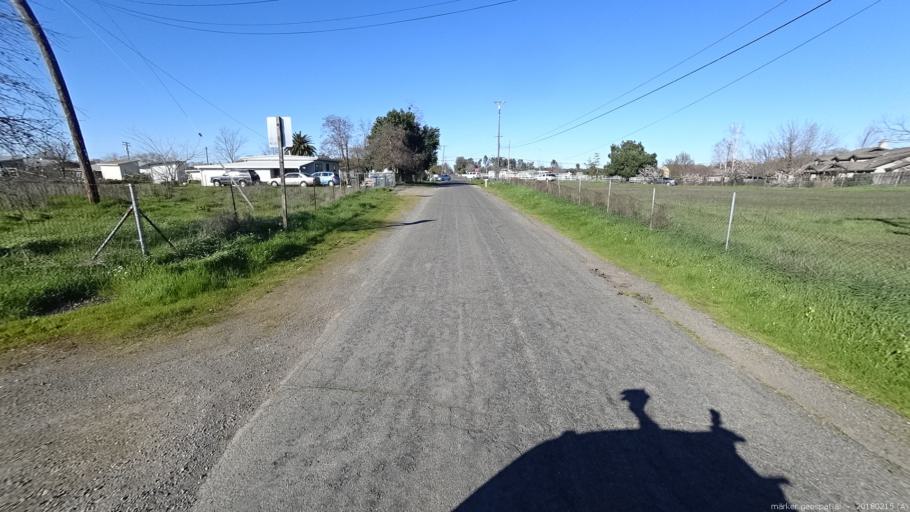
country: US
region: California
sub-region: Sacramento County
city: Rio Linda
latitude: 38.6758
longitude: -121.4615
